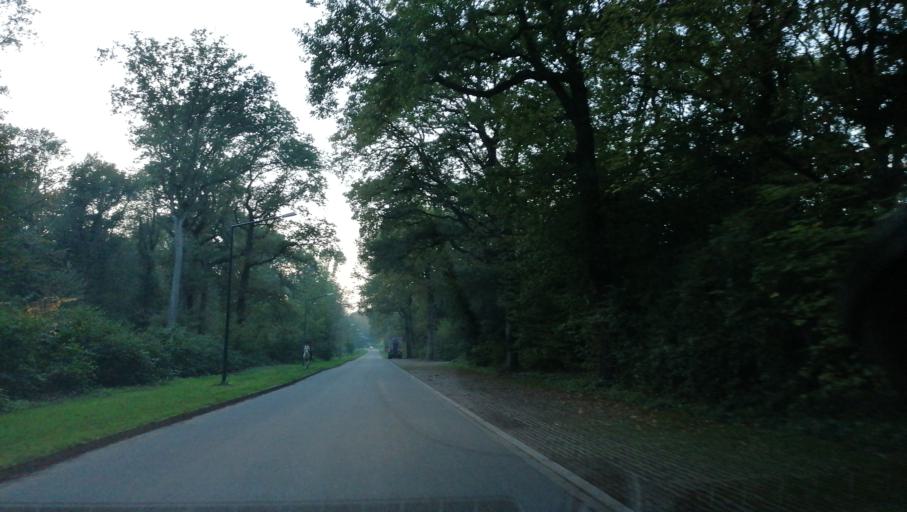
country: DE
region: North Rhine-Westphalia
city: Herten
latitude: 51.5876
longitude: 7.1604
